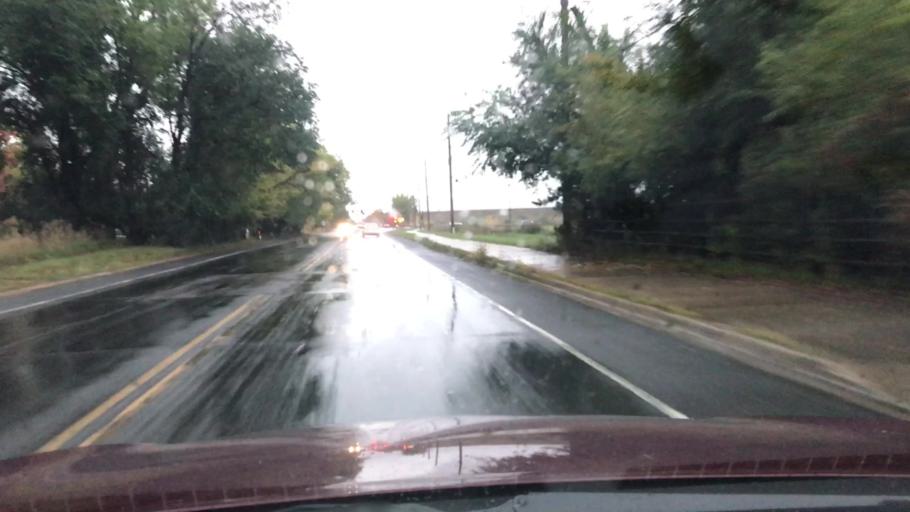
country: US
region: Colorado
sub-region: Boulder County
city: Gunbarrel
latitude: 40.0539
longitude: -105.2069
